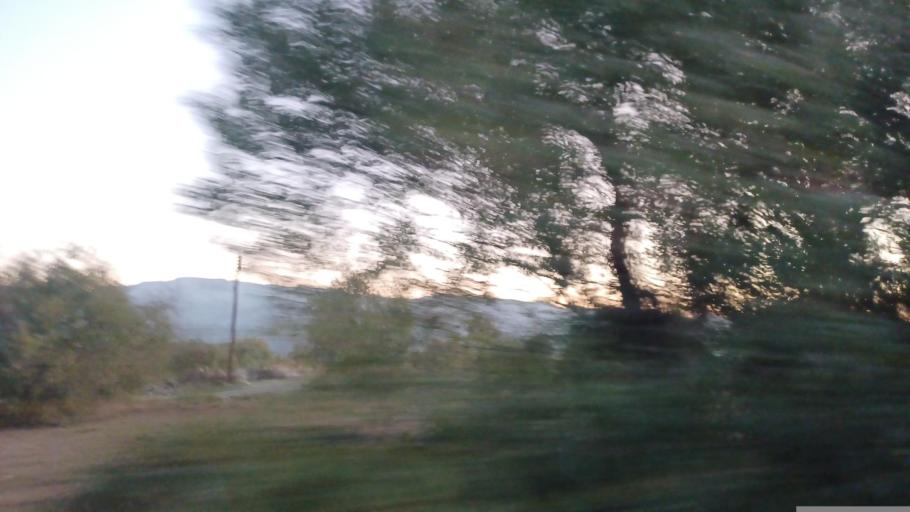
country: CY
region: Pafos
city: Mesogi
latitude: 34.8437
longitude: 32.5302
